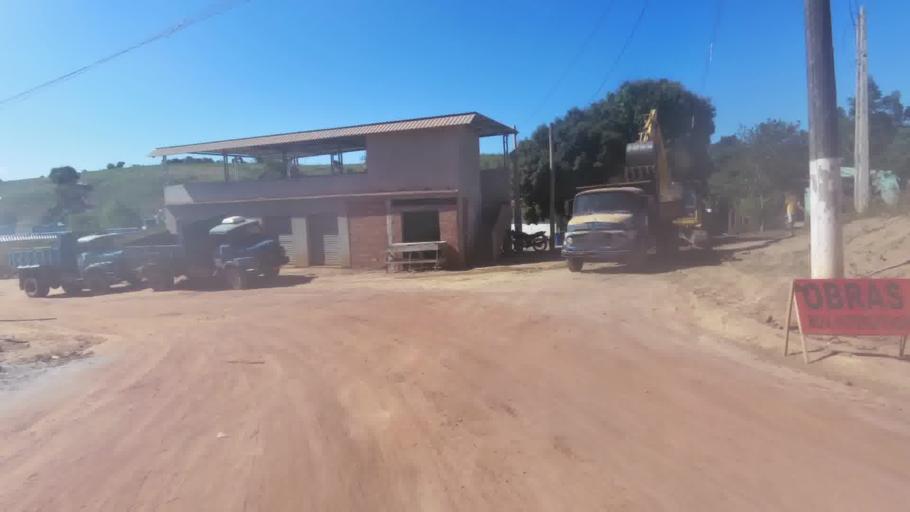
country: BR
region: Espirito Santo
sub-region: Marataizes
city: Marataizes
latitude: -21.1501
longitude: -40.9824
